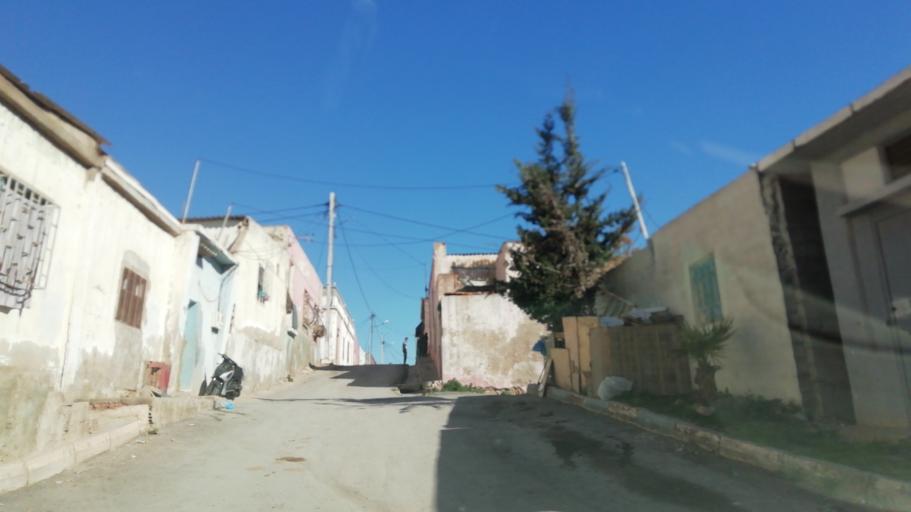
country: DZ
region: Oran
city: Oran
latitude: 35.7030
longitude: -0.6150
